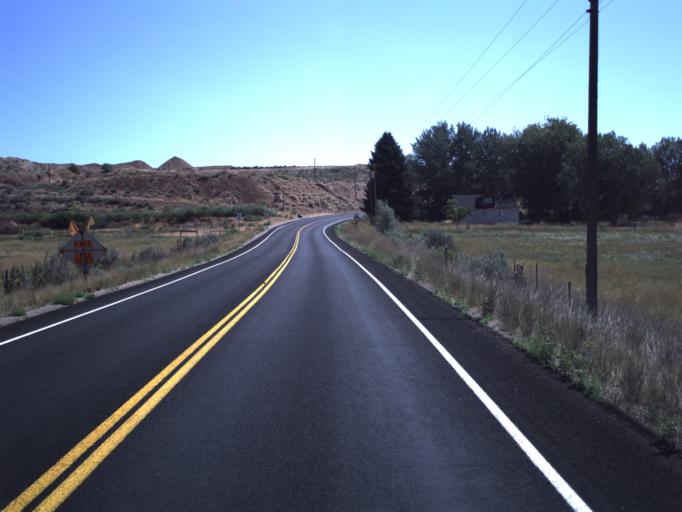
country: US
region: Utah
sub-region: Uintah County
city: Maeser
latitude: 40.4038
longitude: -109.7781
